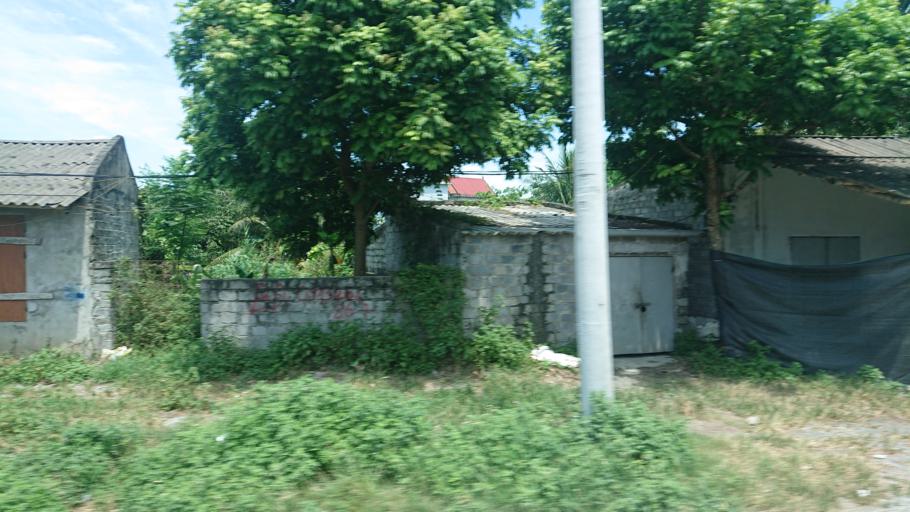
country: VN
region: Ha Nam
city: Thanh Pho Phu Ly
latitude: 20.5231
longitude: 105.9454
